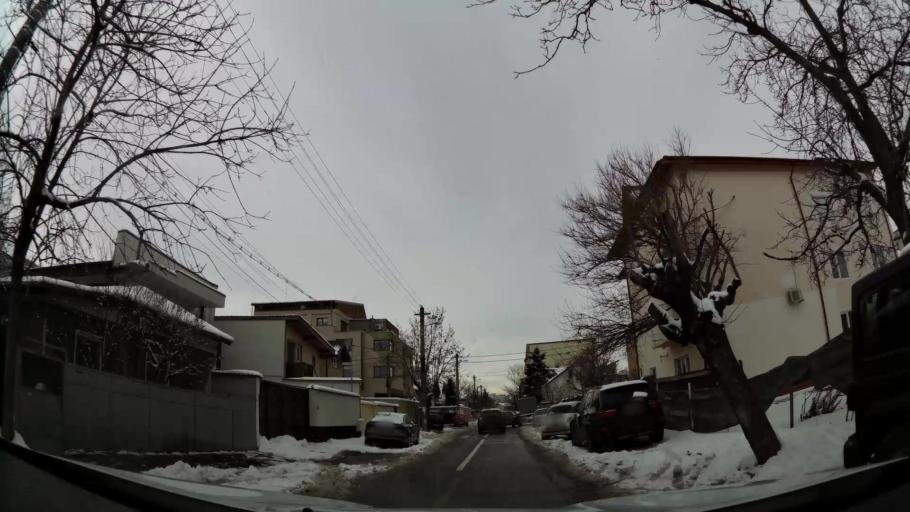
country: RO
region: Bucuresti
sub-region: Municipiul Bucuresti
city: Bucuresti
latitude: 44.3922
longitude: 26.1074
